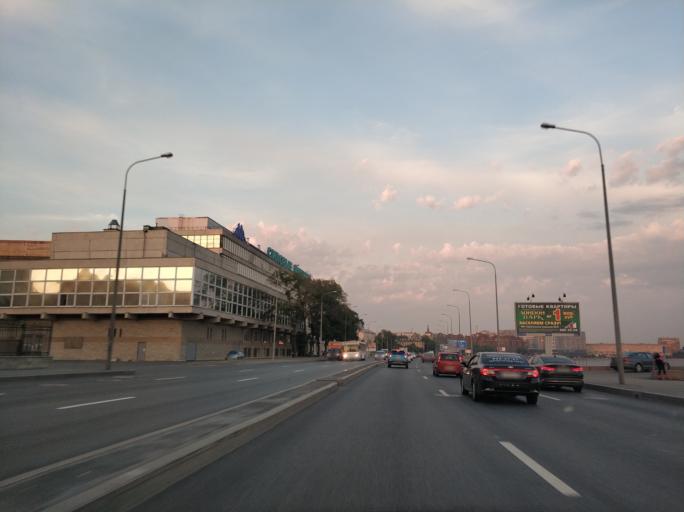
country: RU
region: Leningrad
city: Finlyandskiy
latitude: 59.9598
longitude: 30.3880
